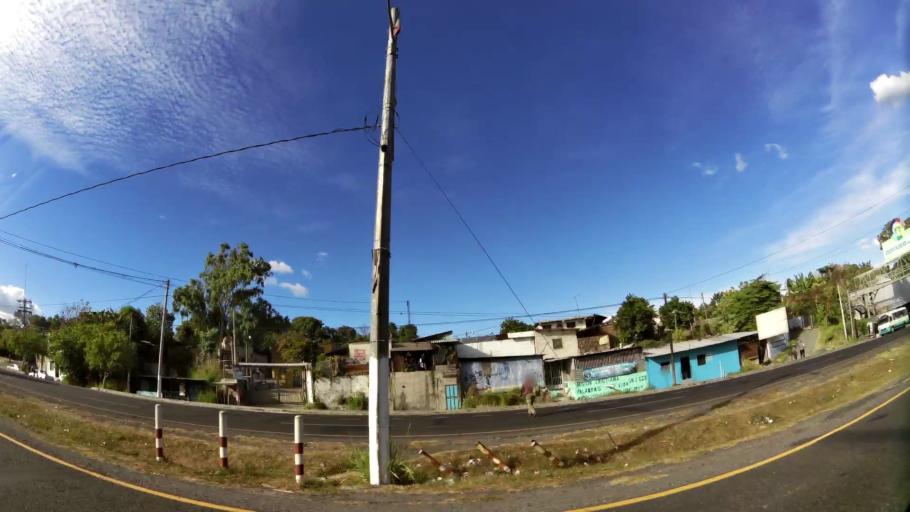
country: SV
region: San Salvador
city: Ilopango
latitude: 13.7338
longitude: -89.0626
